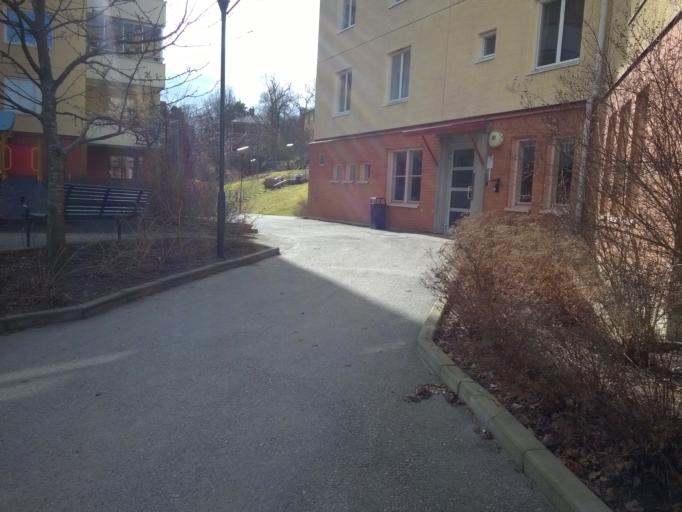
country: SE
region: Stockholm
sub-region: Solna Kommun
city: Solna
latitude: 59.3400
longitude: 17.9883
